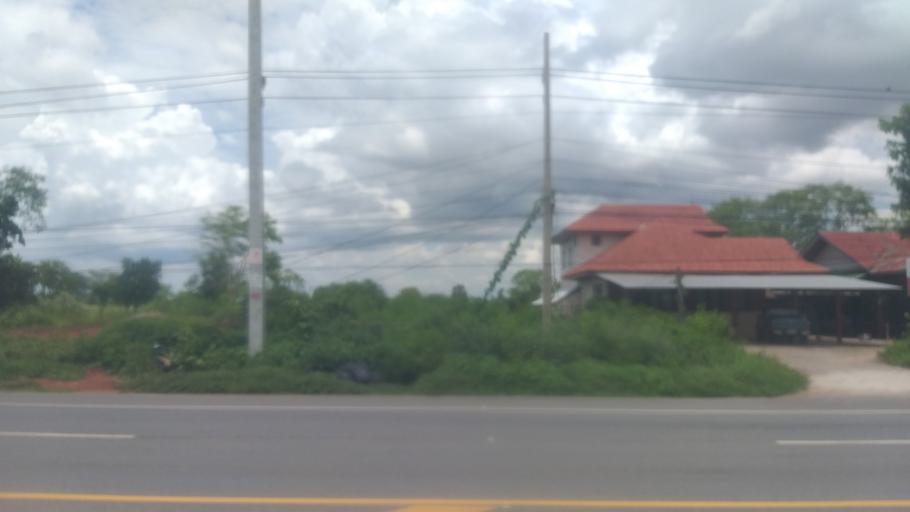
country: TH
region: Nakhon Ratchasima
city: Non Thai
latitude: 15.1131
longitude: 102.1015
